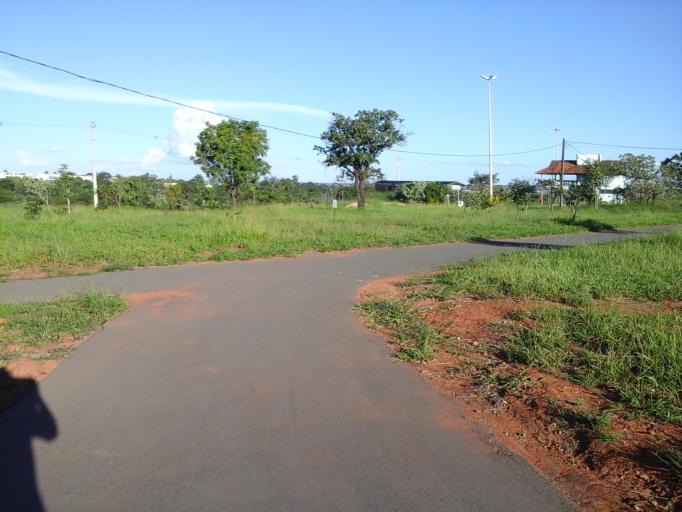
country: BR
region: Federal District
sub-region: Brasilia
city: Brasilia
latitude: -15.8345
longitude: -47.9681
